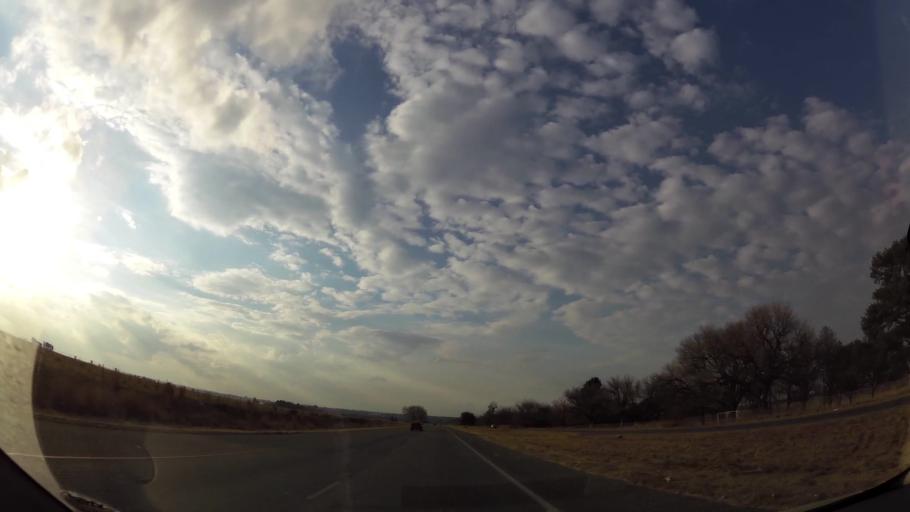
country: ZA
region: Orange Free State
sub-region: Fezile Dabi District Municipality
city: Sasolburg
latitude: -26.7718
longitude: 27.8251
